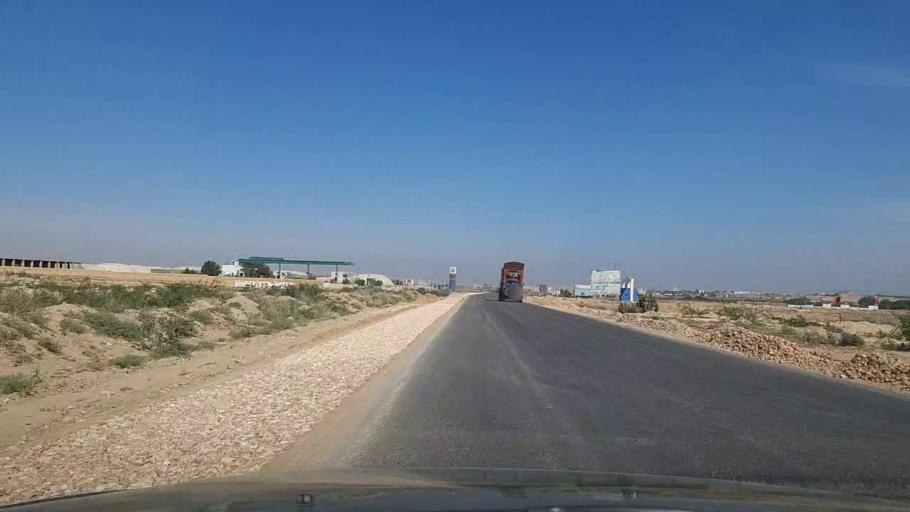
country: PK
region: Sindh
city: Kotri
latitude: 25.3237
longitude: 68.2351
